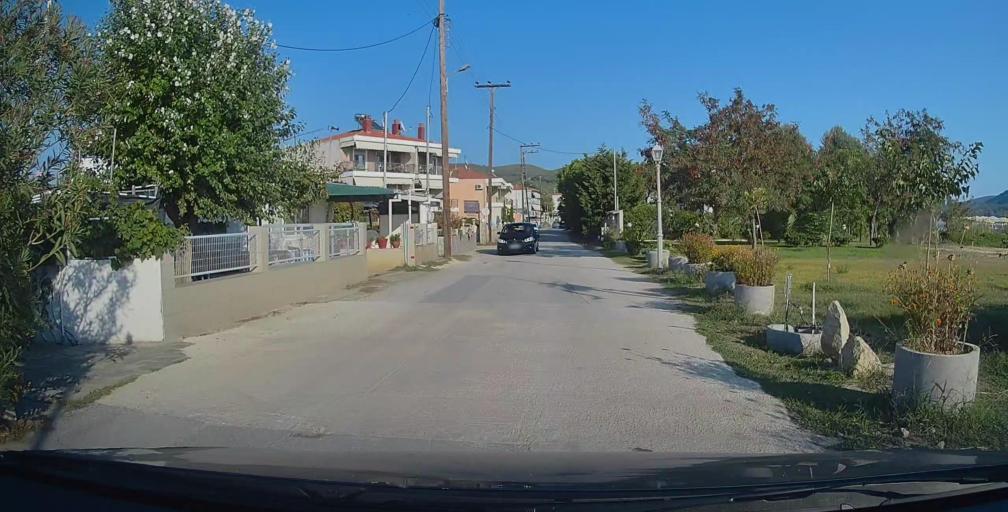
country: GR
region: Central Macedonia
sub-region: Nomos Chalkidikis
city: Sykia
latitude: 39.9899
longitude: 23.8960
